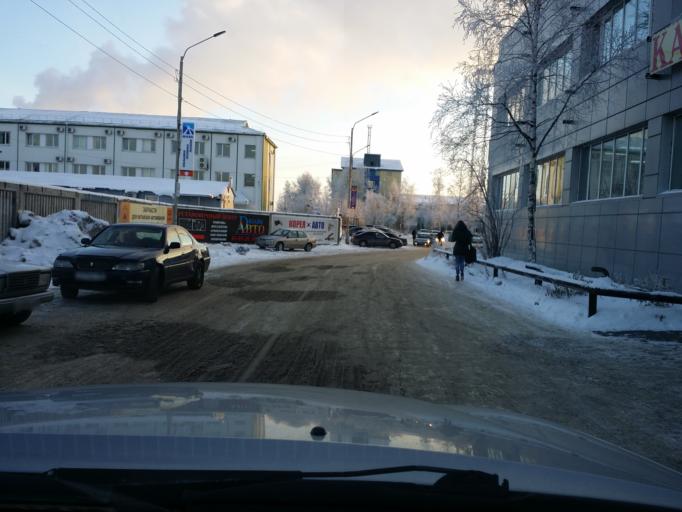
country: RU
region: Khanty-Mansiyskiy Avtonomnyy Okrug
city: Nizhnevartovsk
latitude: 60.9404
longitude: 76.5382
